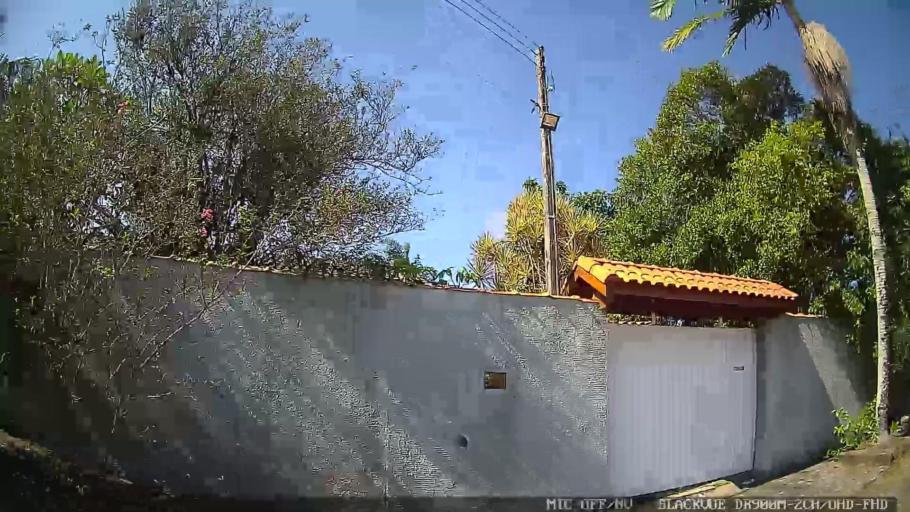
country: BR
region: Sao Paulo
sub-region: Peruibe
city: Peruibe
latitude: -24.3068
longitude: -46.9867
